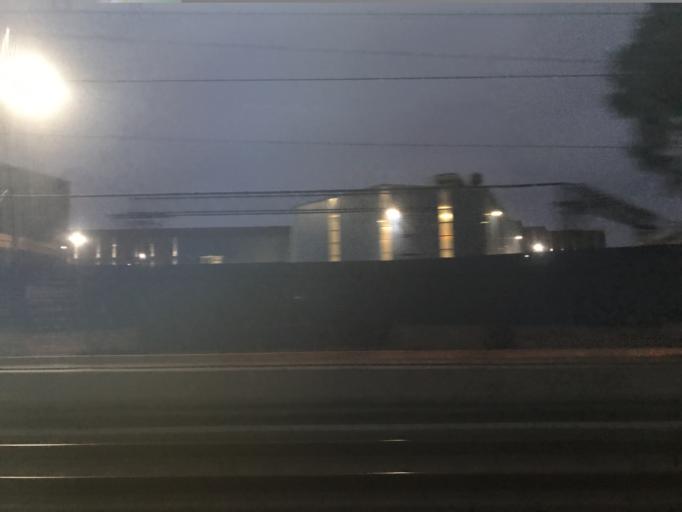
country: TR
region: Kocaeli
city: Darica
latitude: 40.8031
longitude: 29.3740
